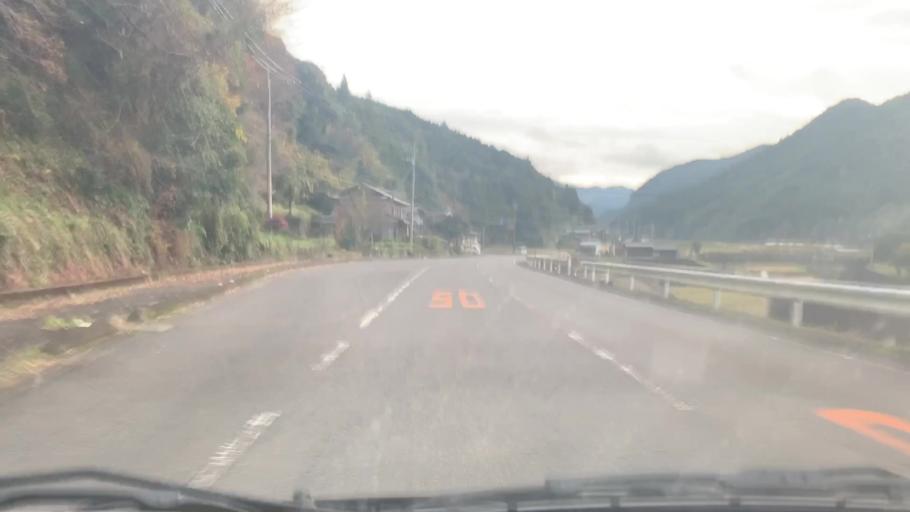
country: JP
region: Saga Prefecture
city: Kashima
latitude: 33.0657
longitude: 130.0704
